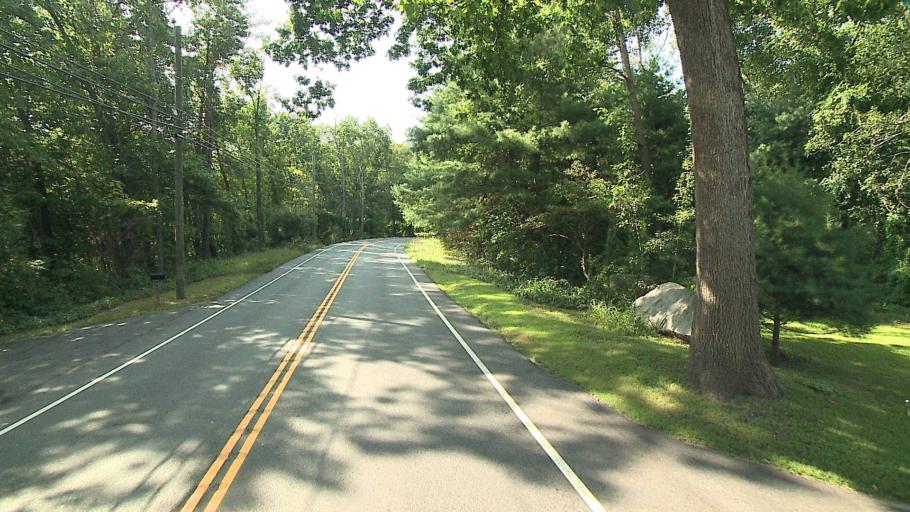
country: US
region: Connecticut
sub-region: Fairfield County
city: Sherman
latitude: 41.6115
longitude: -73.4514
